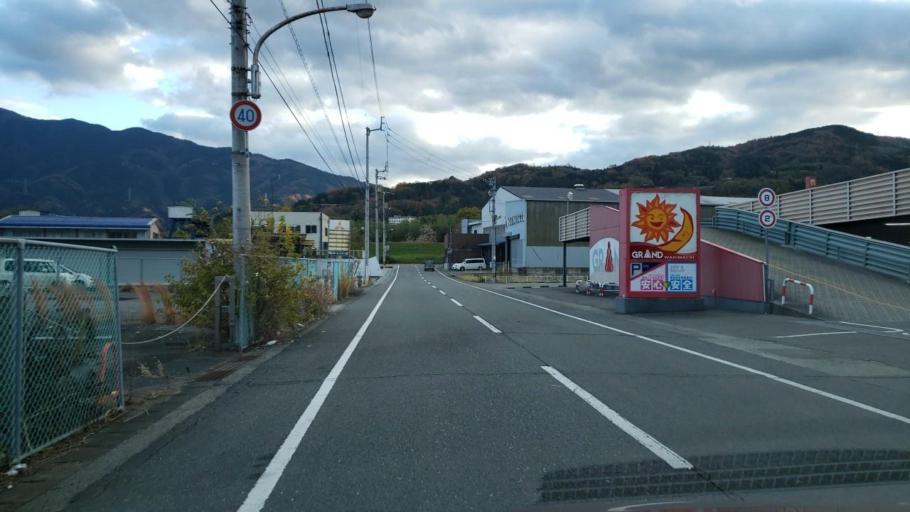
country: JP
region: Tokushima
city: Wakimachi
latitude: 34.0626
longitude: 134.1635
